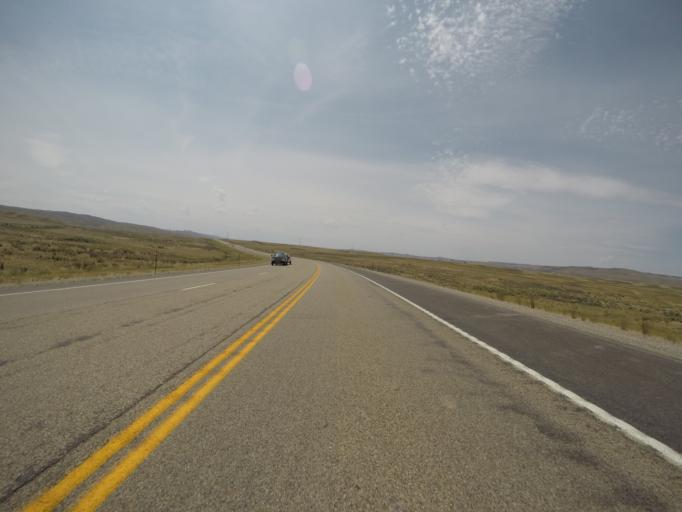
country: US
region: Wyoming
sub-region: Lincoln County
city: Kemmerer
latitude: 41.7531
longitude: -110.5650
